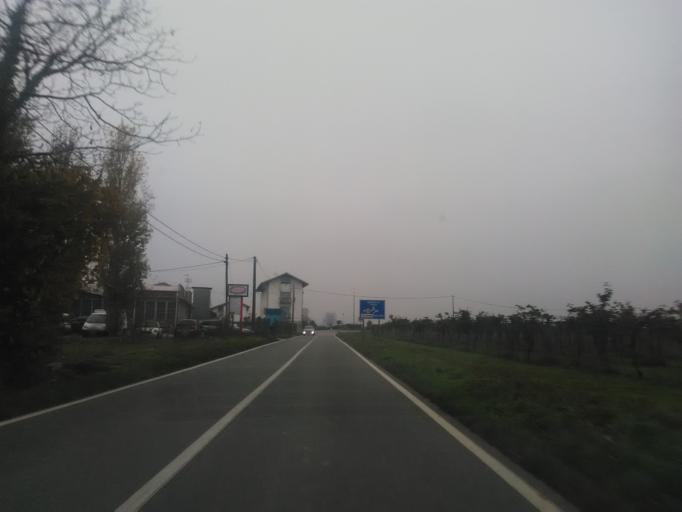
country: IT
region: Piedmont
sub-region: Provincia di Vercelli
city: Cigliano
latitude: 45.3196
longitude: 8.0195
